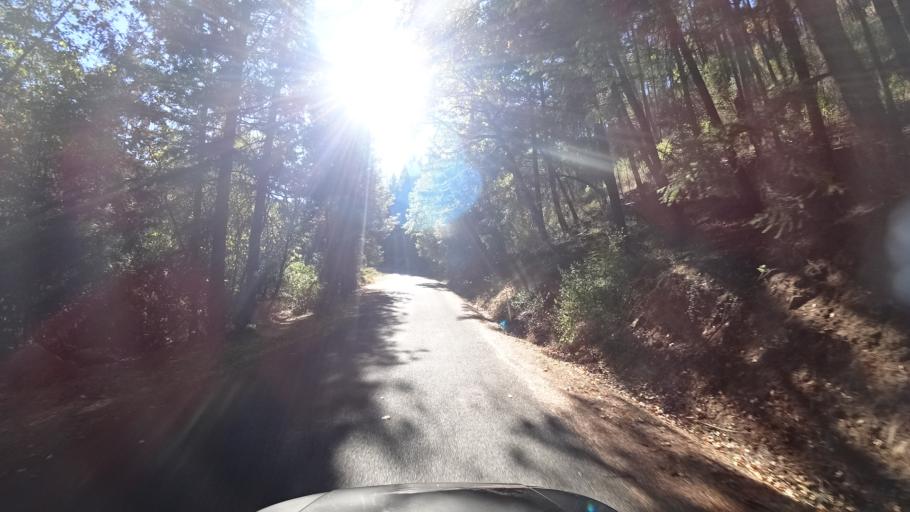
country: US
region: California
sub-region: Humboldt County
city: Willow Creek
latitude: 41.2892
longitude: -123.2502
